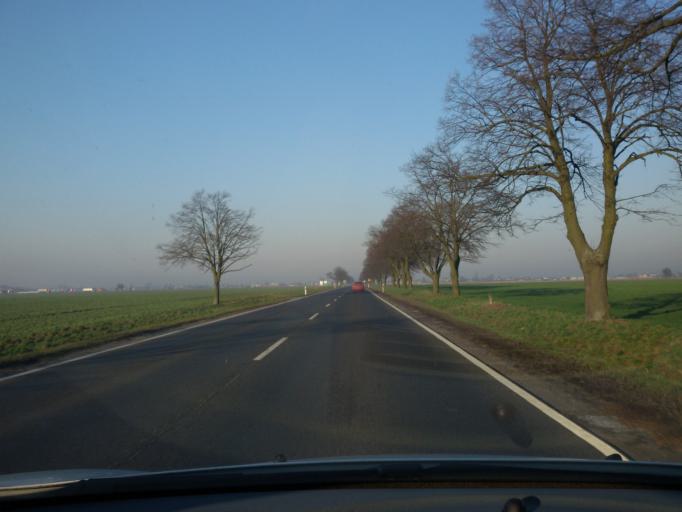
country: PL
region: Greater Poland Voivodeship
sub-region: Powiat leszczynski
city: Swieciechowa
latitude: 51.8286
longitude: 16.5116
